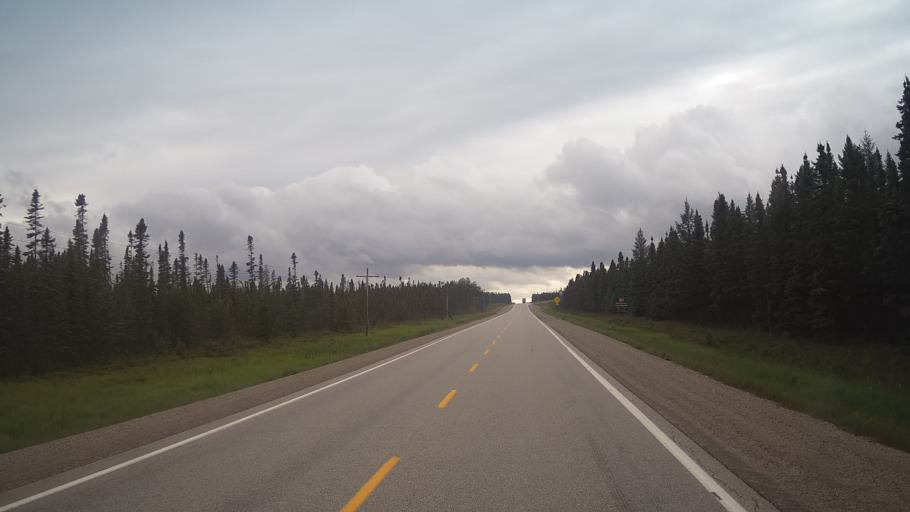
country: CA
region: Ontario
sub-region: Thunder Bay District
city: Thunder Bay
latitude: 48.9438
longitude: -90.1781
